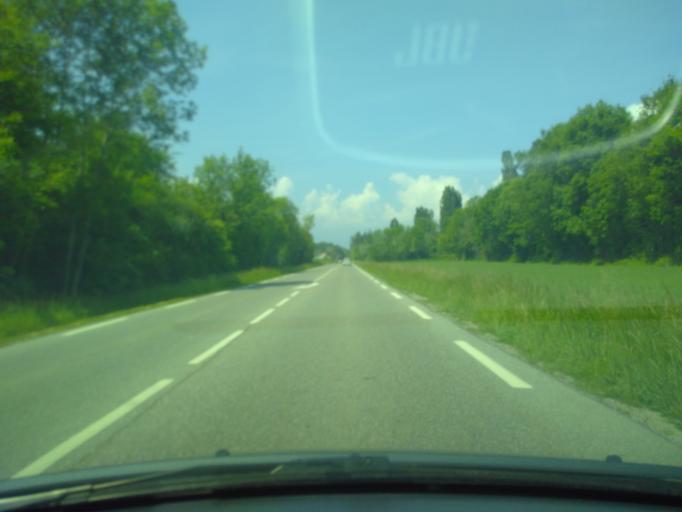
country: FR
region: Rhone-Alpes
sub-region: Departement de la Haute-Savoie
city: Archamps
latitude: 46.1423
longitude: 6.1196
